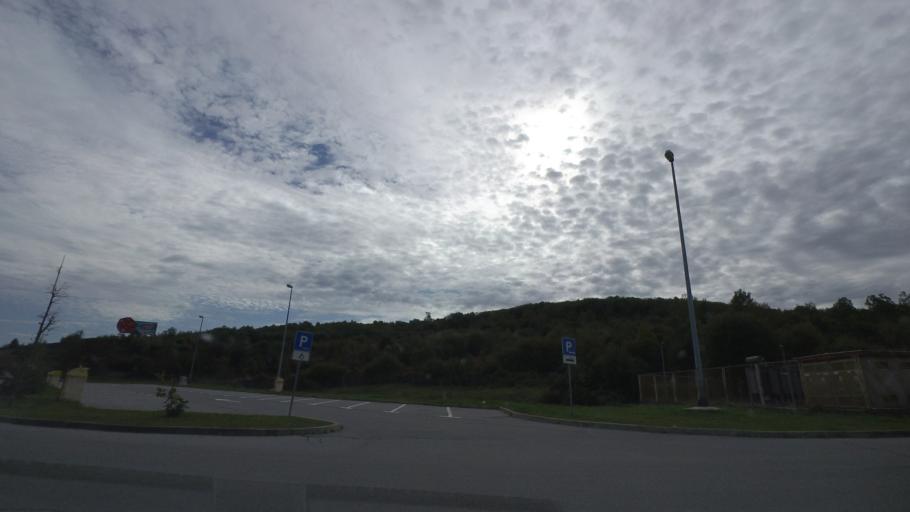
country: HR
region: Licko-Senjska
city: Otocac
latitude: 44.9207
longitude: 15.1669
